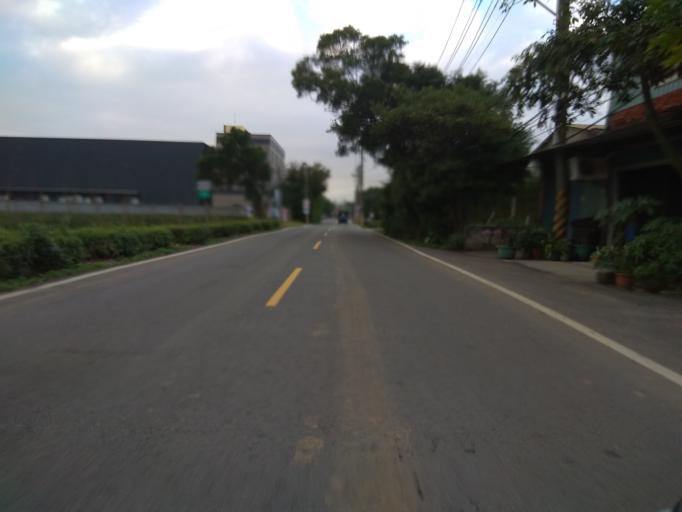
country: TW
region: Taiwan
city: Daxi
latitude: 24.8436
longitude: 121.2013
